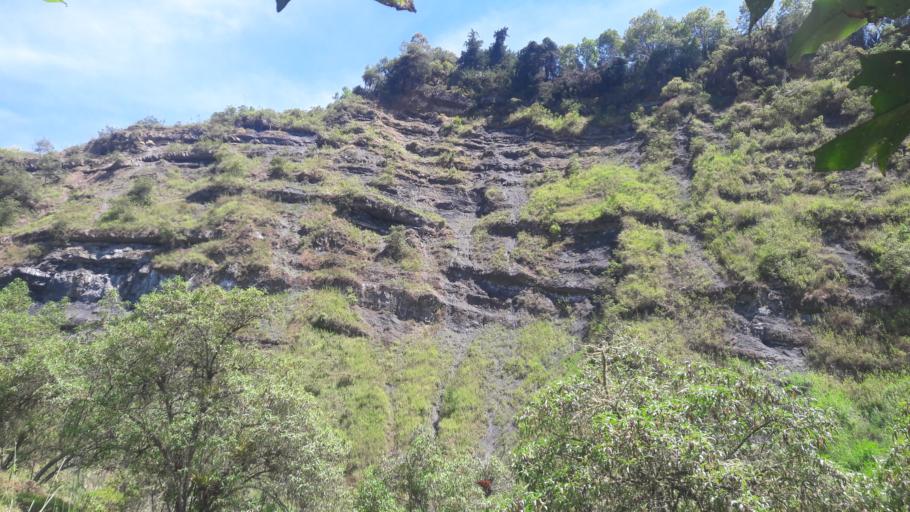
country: CO
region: Cundinamarca
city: Tenza
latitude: 5.0896
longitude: -73.4095
